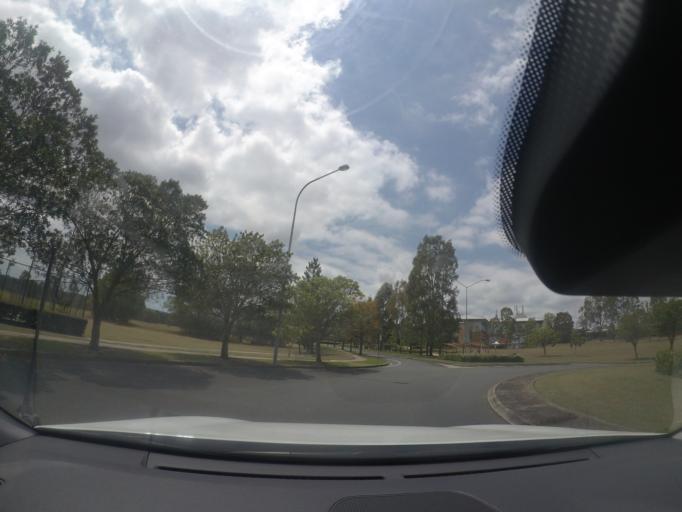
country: AU
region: Queensland
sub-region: Logan
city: Slacks Creek
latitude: -27.6643
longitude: 153.1506
